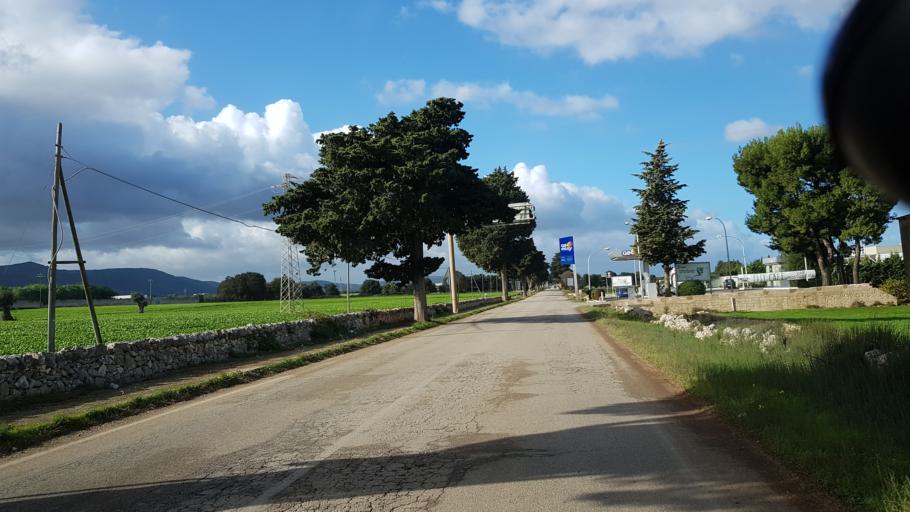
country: IT
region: Apulia
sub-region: Provincia di Brindisi
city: Montalbano
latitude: 40.7839
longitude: 17.4770
